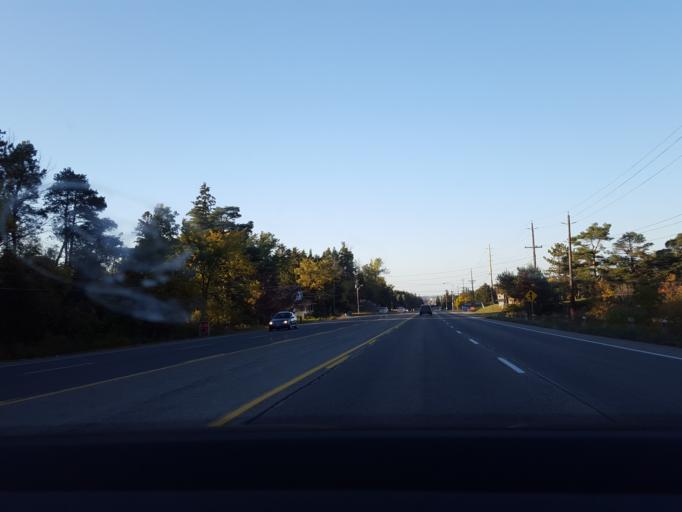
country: CA
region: Ontario
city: Newmarket
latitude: 43.9705
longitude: -79.4606
